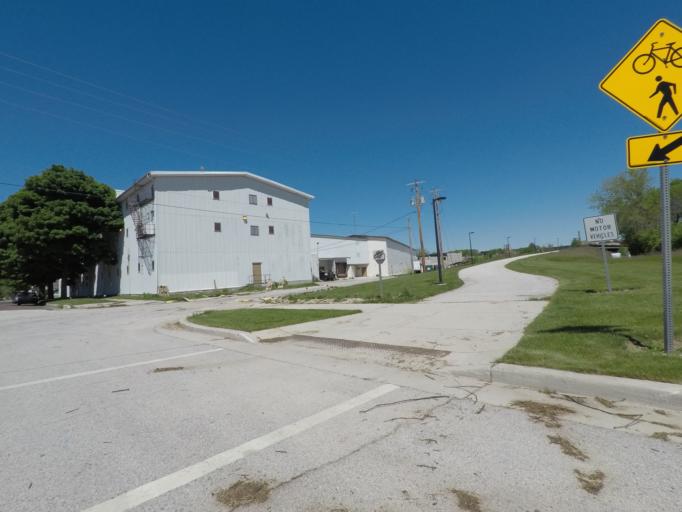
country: US
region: Wisconsin
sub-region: Sheboygan County
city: Sheboygan
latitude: 43.7531
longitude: -87.7211
